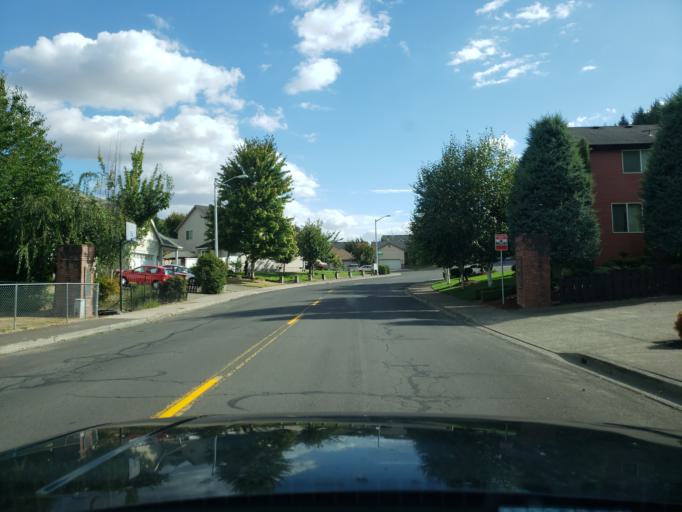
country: US
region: Oregon
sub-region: Yamhill County
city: McMinnville
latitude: 45.2134
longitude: -123.2188
